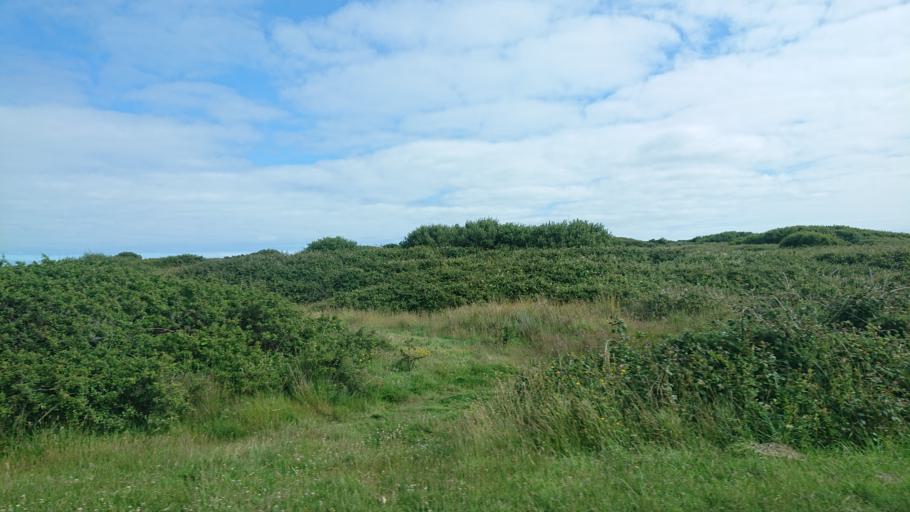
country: FR
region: Brittany
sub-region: Departement du Finistere
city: Porspoder
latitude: 48.4671
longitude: -5.0638
